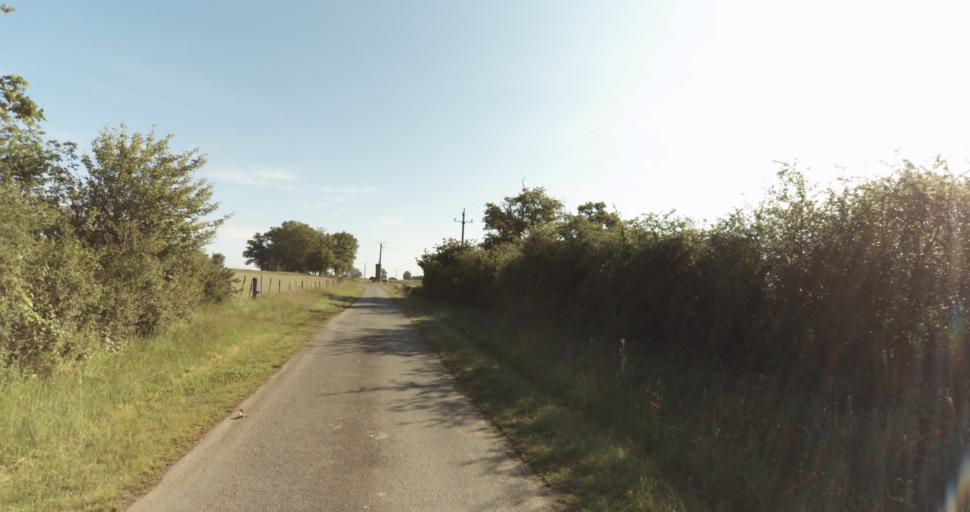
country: FR
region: Limousin
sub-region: Departement de la Haute-Vienne
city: Solignac
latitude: 45.7408
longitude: 1.2662
